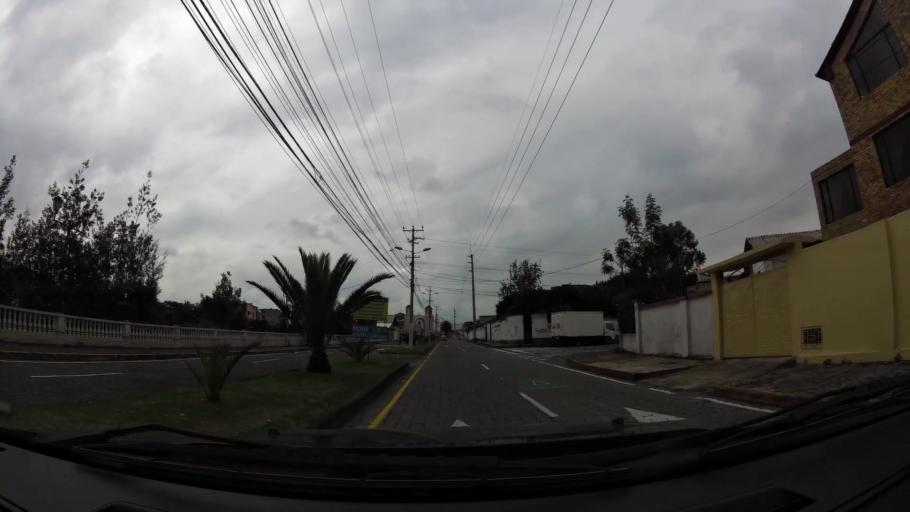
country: EC
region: Pichincha
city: Sangolqui
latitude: -0.3063
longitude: -78.4572
